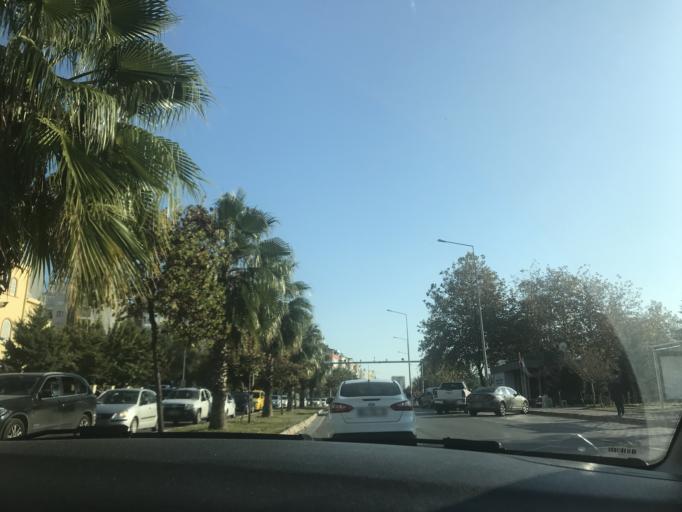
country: TR
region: Antalya
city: Antalya
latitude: 36.8825
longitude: 30.6488
